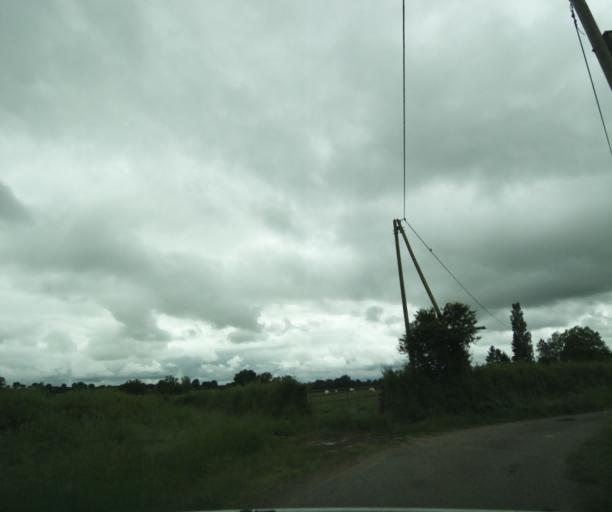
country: FR
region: Bourgogne
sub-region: Departement de Saone-et-Loire
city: Charolles
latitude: 46.4740
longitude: 4.3211
